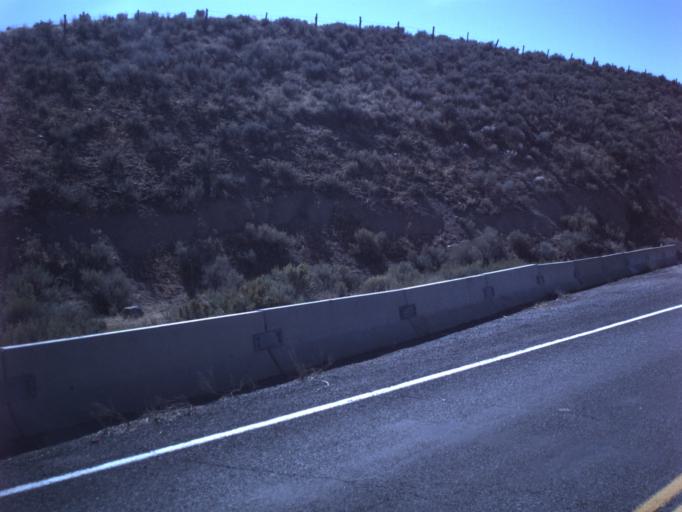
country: US
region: Utah
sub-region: Juab County
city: Nephi
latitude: 39.4872
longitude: -111.9704
